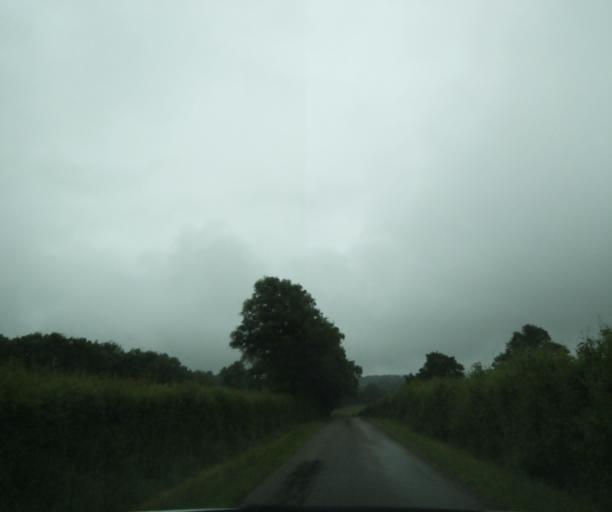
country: FR
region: Bourgogne
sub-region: Departement de Saone-et-Loire
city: Charolles
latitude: 46.4508
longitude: 4.2098
